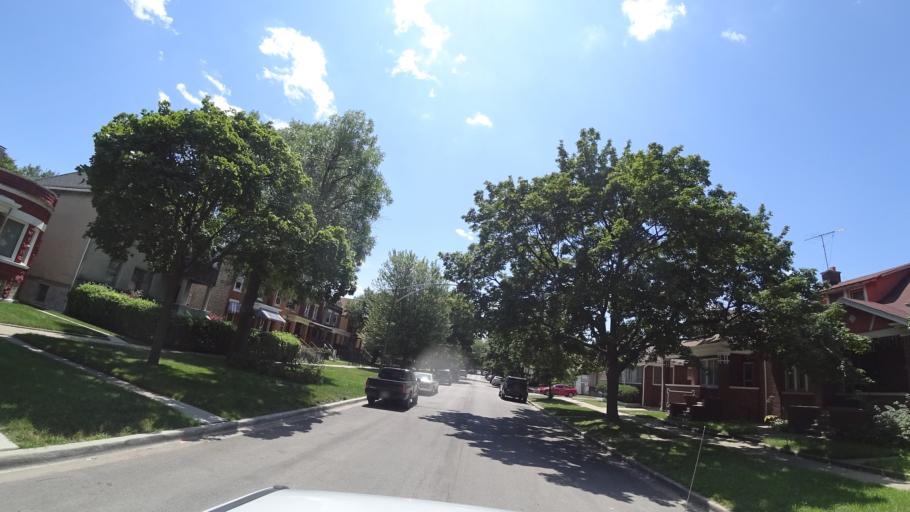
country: US
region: Illinois
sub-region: Cook County
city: Chicago
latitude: 41.7688
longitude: -87.6170
